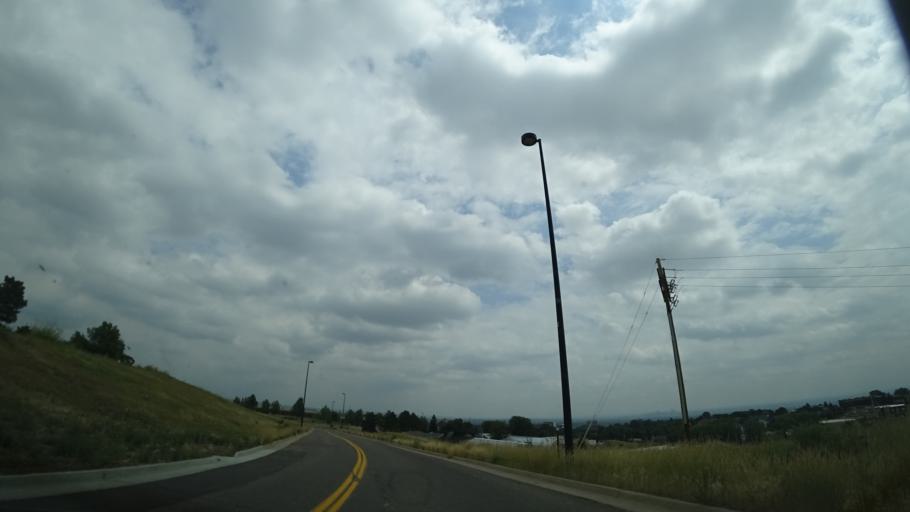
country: US
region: Colorado
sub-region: Jefferson County
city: West Pleasant View
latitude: 39.7122
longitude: -105.1516
